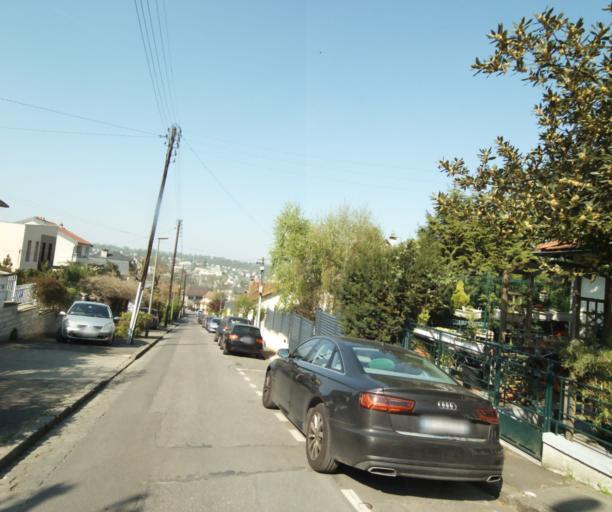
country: FR
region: Ile-de-France
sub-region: Departement des Hauts-de-Seine
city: Ville-d'Avray
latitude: 48.8172
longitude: 2.2047
